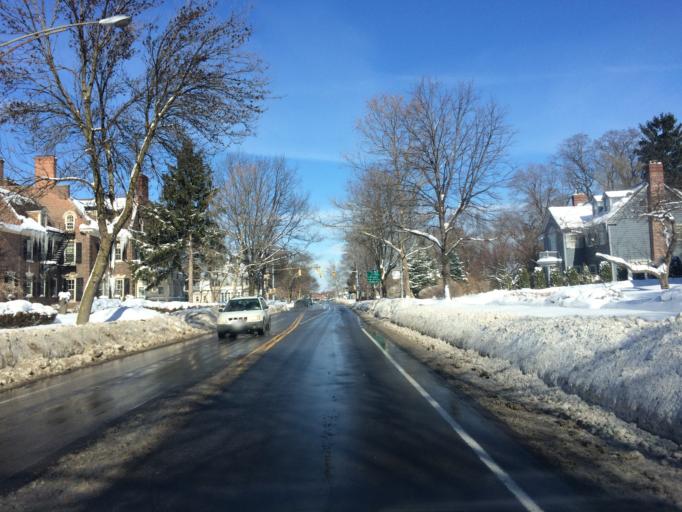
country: US
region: New York
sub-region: Monroe County
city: Brighton
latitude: 43.1486
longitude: -77.5722
